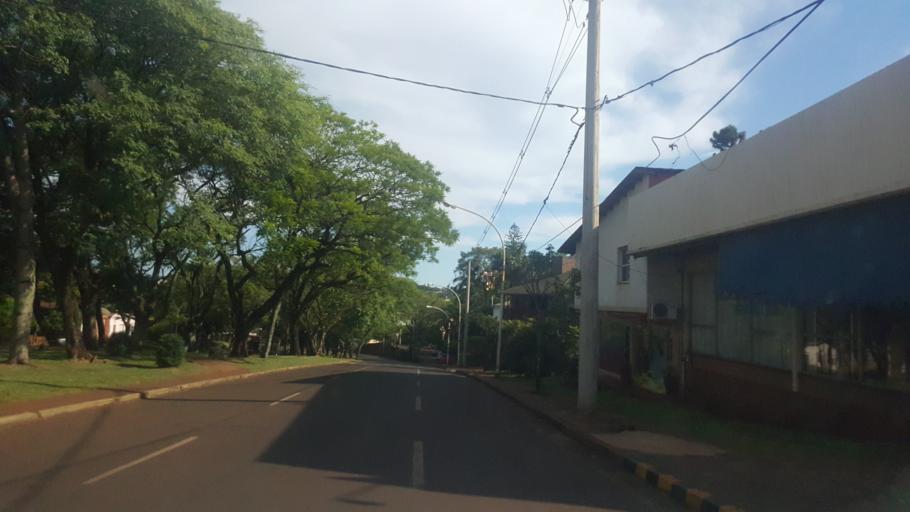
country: AR
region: Misiones
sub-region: Departamento de Leandro N. Alem
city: Leandro N. Alem
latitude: -27.6050
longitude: -55.3207
